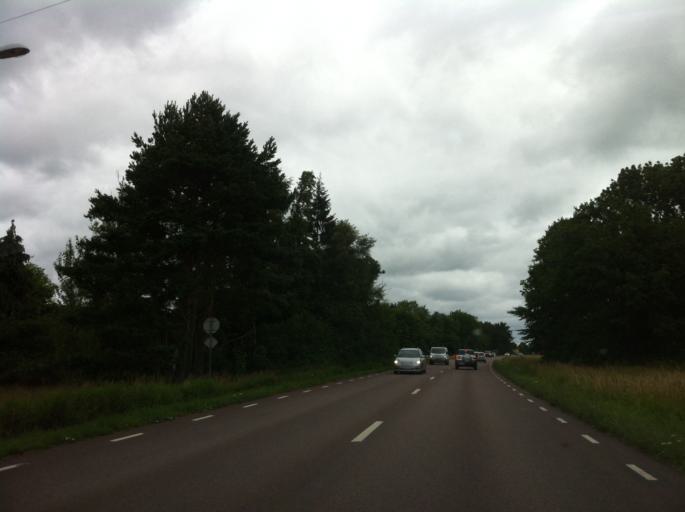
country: SE
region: Kalmar
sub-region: Borgholms Kommun
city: Borgholm
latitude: 57.1843
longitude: 17.0294
